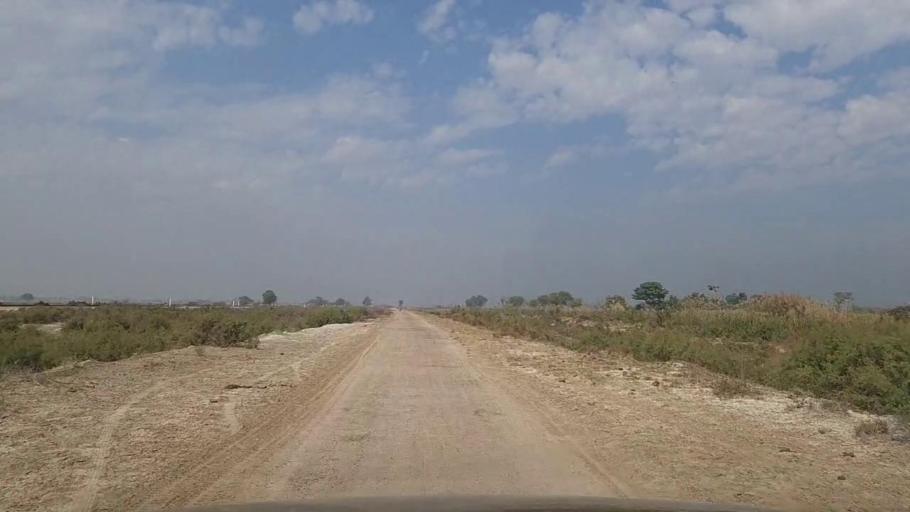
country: PK
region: Sindh
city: Daur
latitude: 26.3925
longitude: 68.3495
